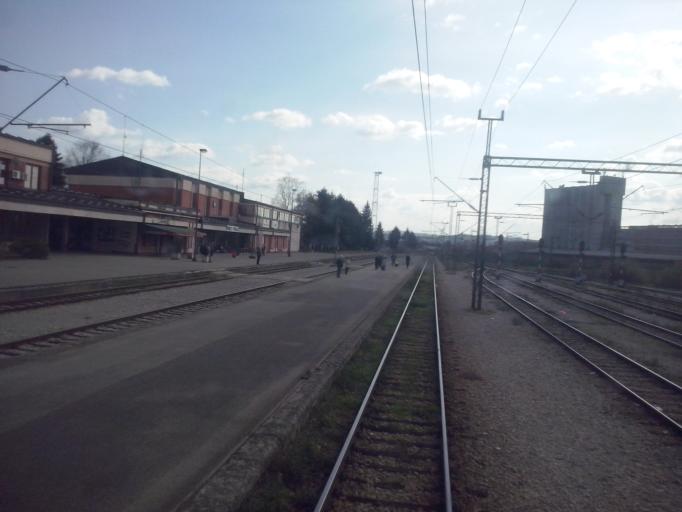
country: RS
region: Central Serbia
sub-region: Zlatiborski Okrug
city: Pozega
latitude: 43.8410
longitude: 20.0280
